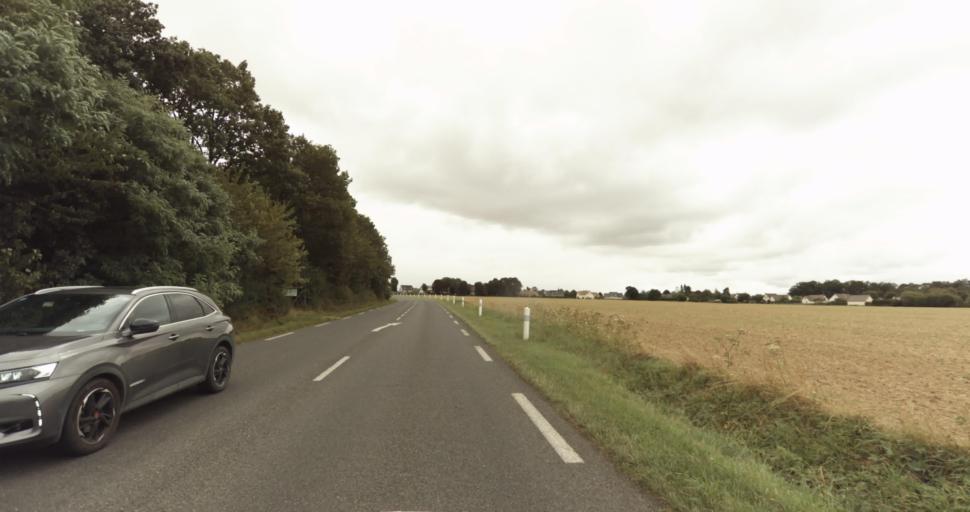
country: FR
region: Haute-Normandie
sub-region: Departement de l'Eure
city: Evreux
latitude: 48.9860
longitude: 1.1881
